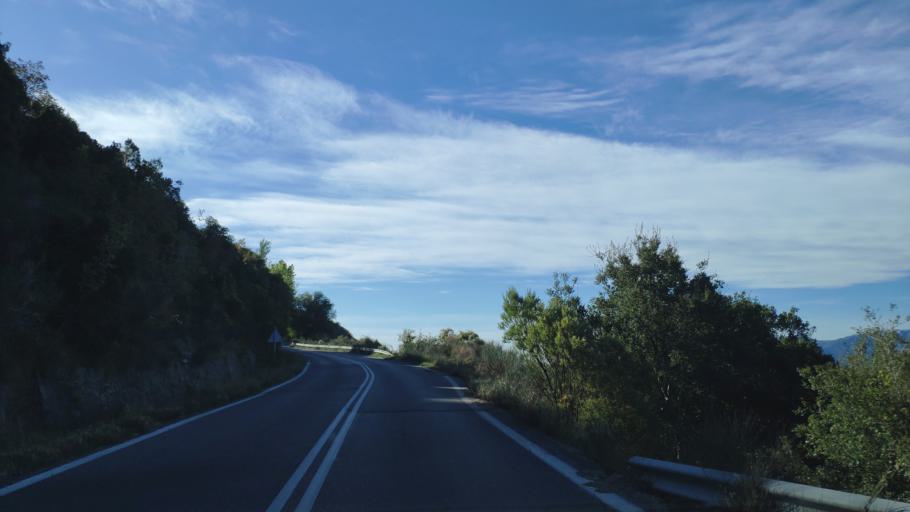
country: GR
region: Peloponnese
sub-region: Nomos Arkadias
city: Dimitsana
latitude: 37.5619
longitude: 22.0624
